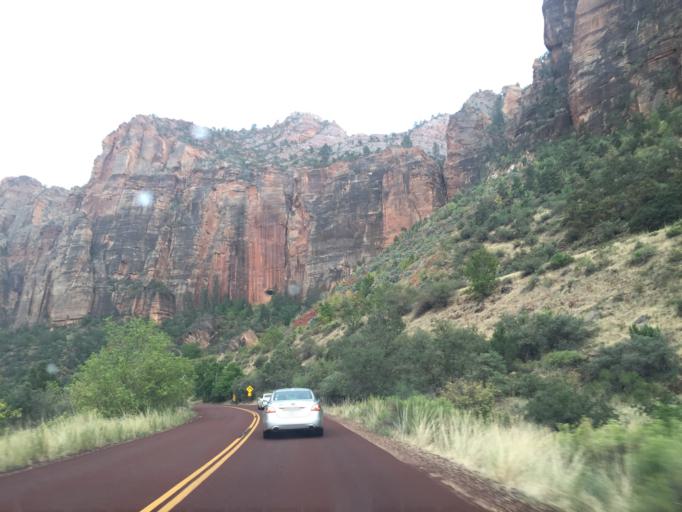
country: US
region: Utah
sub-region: Washington County
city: Hildale
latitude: 37.2130
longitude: -112.9586
